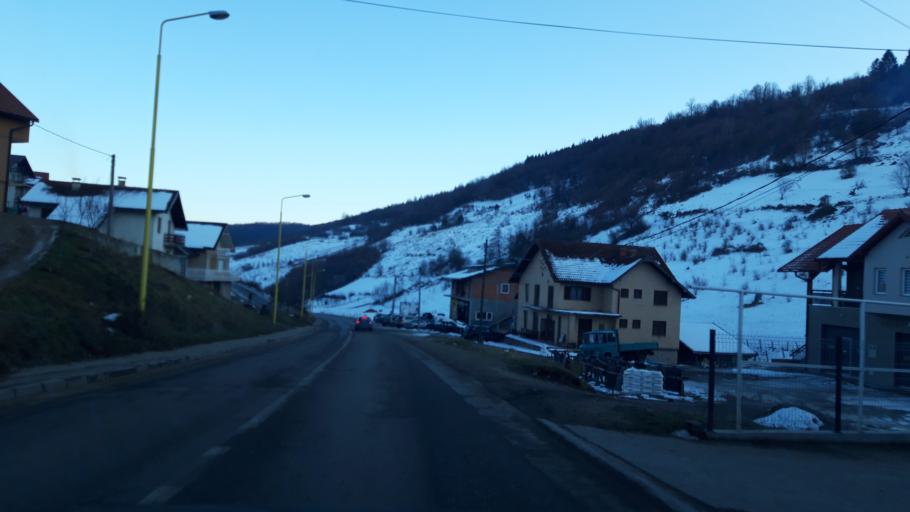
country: BA
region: Republika Srpska
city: Vlasenica
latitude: 44.1815
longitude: 18.9499
